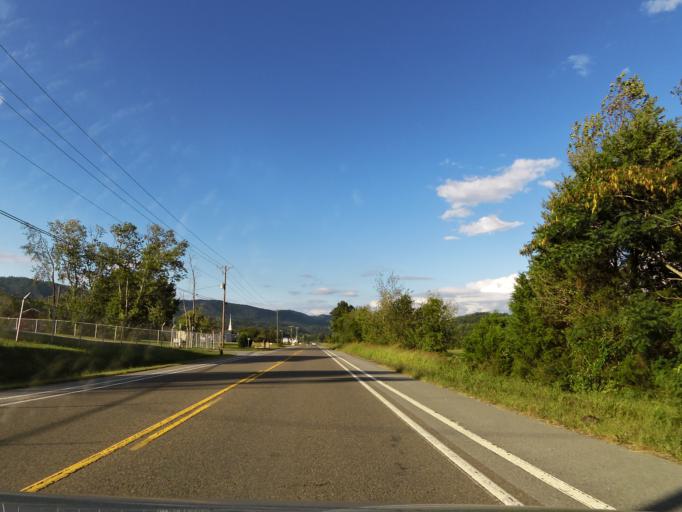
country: US
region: Tennessee
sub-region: Grainger County
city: Blaine
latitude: 36.1788
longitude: -83.6821
